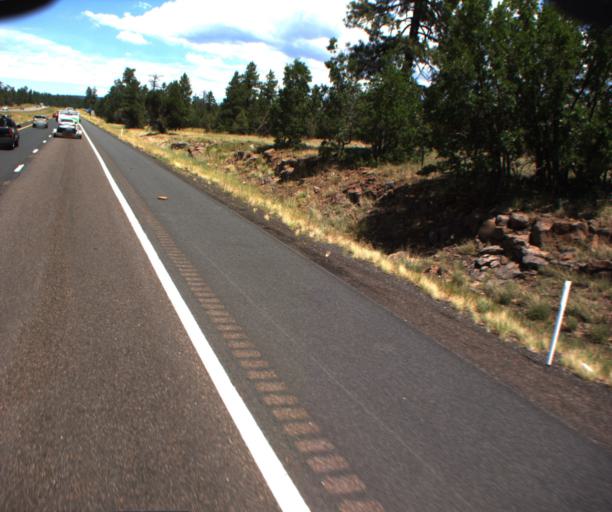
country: US
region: Arizona
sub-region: Coconino County
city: Sedona
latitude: 34.9209
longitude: -111.6435
